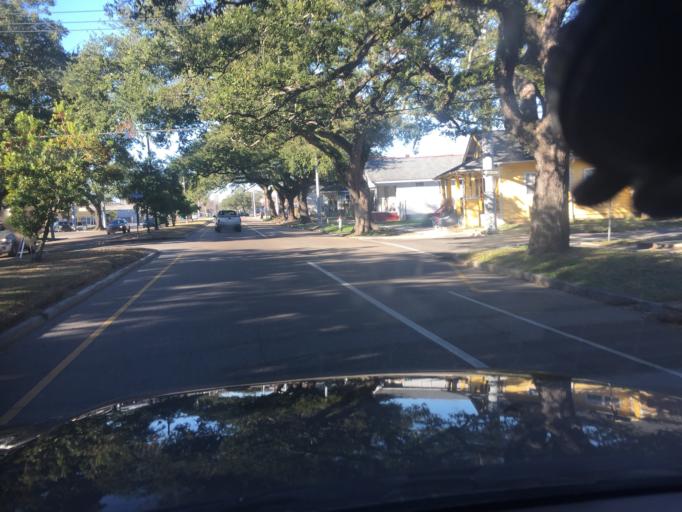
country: US
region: Louisiana
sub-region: Orleans Parish
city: New Orleans
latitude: 29.9807
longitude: -90.0702
